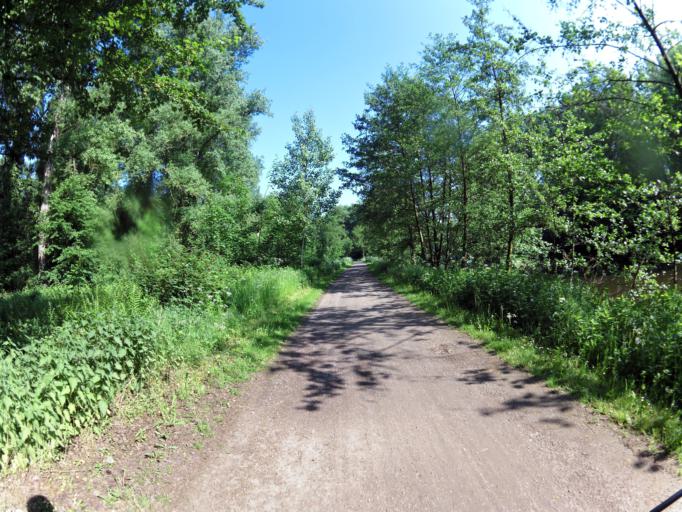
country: DE
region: North Rhine-Westphalia
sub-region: Regierungsbezirk Koln
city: Linnich
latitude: 50.9688
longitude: 6.2784
